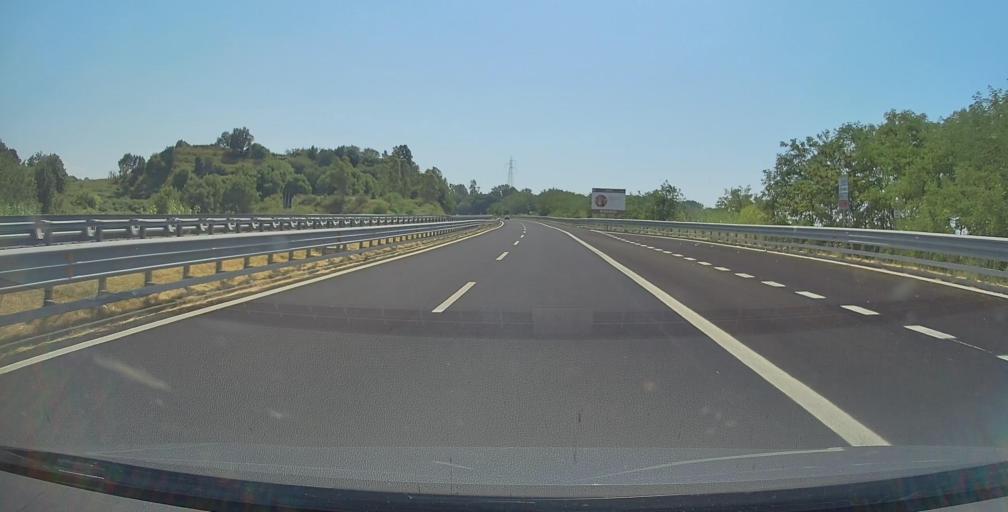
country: IT
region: Calabria
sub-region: Provincia di Reggio Calabria
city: Rosarno
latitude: 38.4975
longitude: 16.0176
